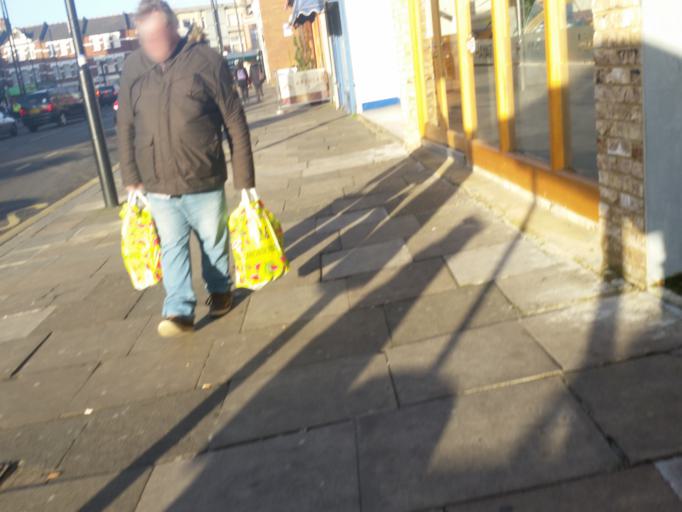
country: GB
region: England
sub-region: Greater London
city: Wood Green
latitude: 51.6168
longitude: -0.1091
